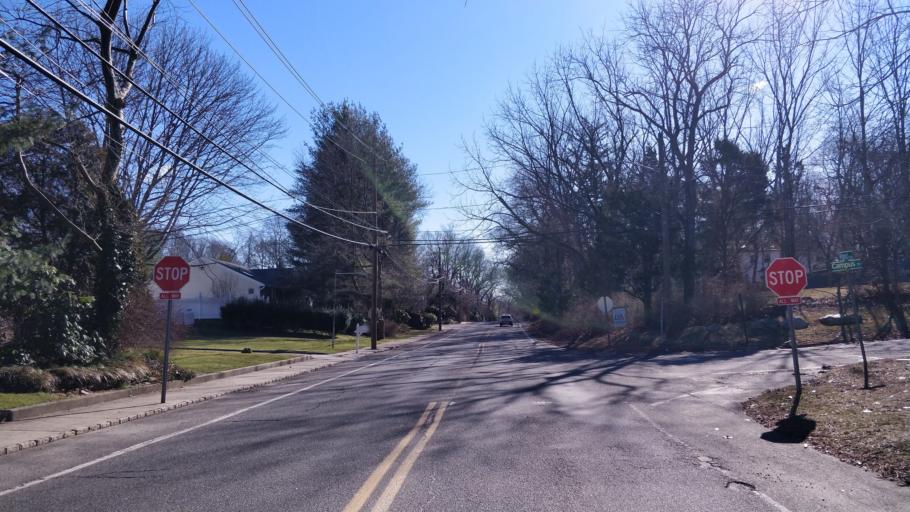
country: US
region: New York
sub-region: Suffolk County
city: Setauket-East Setauket
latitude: 40.9086
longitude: -73.1015
